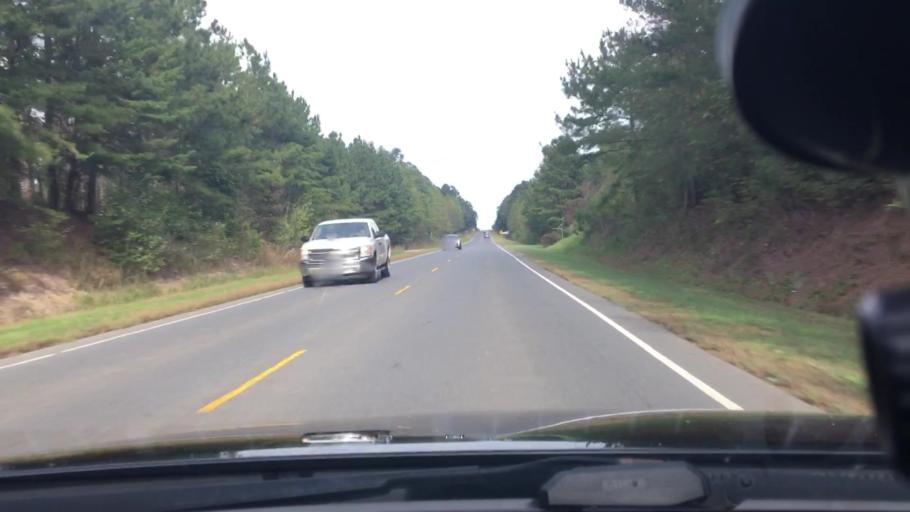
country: US
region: North Carolina
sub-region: Montgomery County
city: Troy
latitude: 35.3156
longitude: -79.9800
